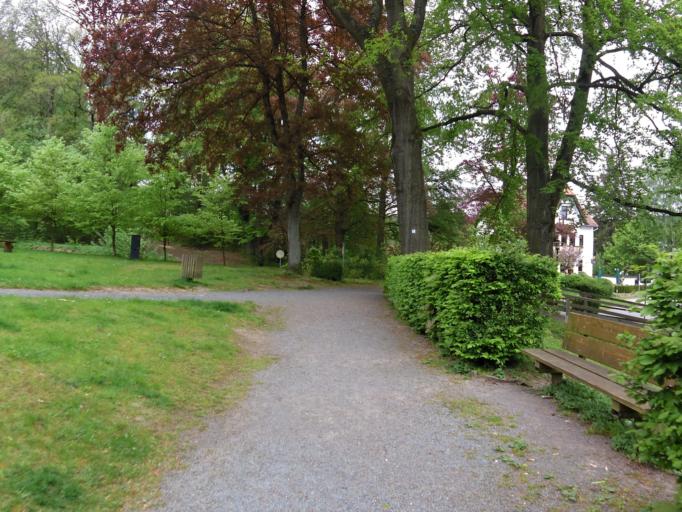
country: DE
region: Thuringia
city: Georgenthal
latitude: 50.8277
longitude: 10.6574
